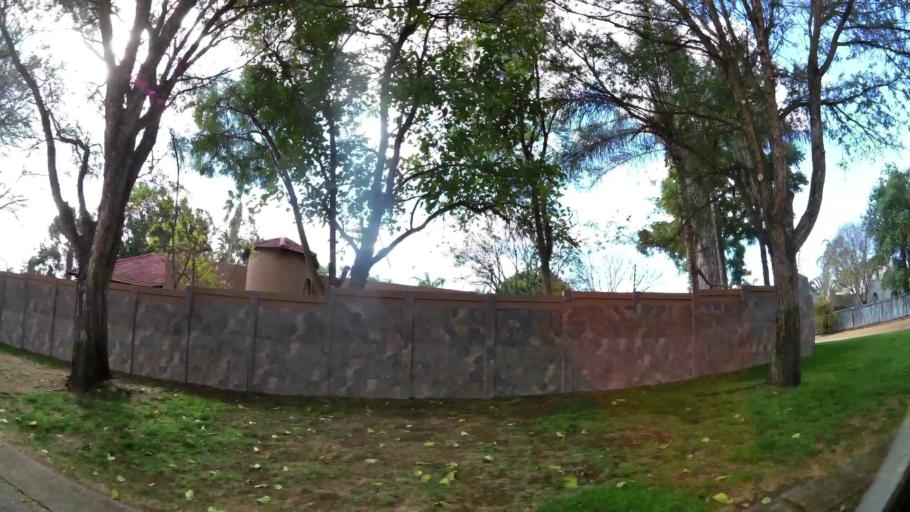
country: ZA
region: Limpopo
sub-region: Capricorn District Municipality
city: Polokwane
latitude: -23.8914
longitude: 29.4792
